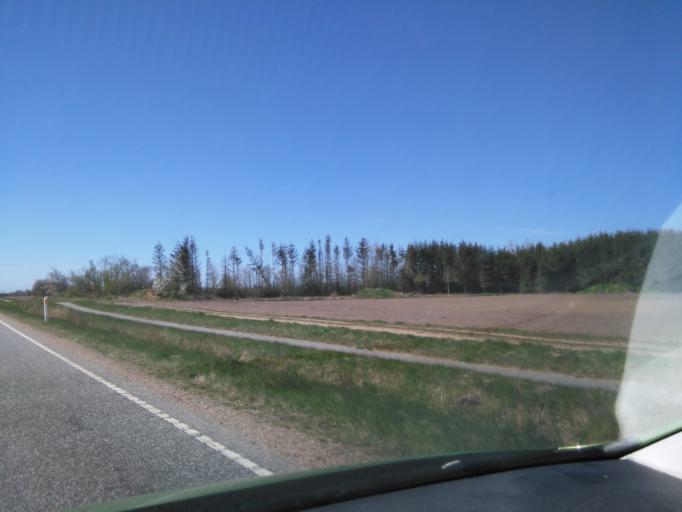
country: DK
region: South Denmark
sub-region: Varde Kommune
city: Oksbol
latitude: 55.6204
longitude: 8.3558
